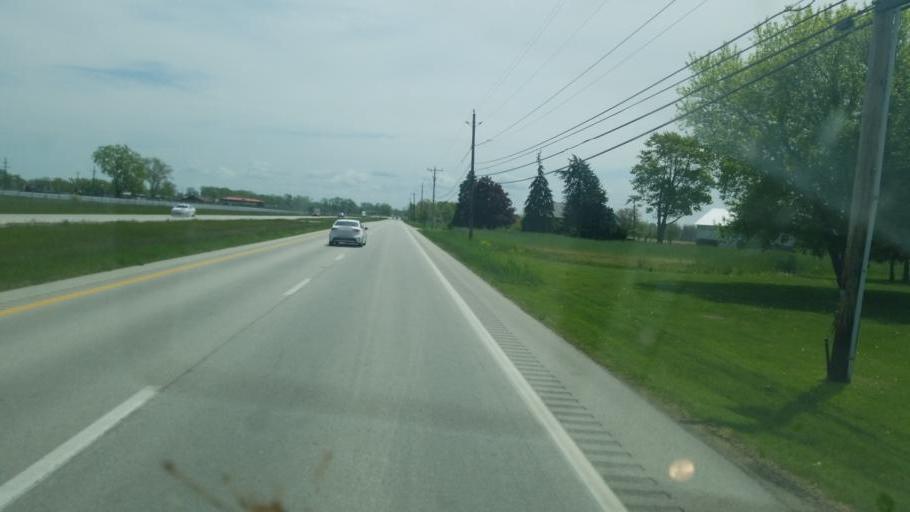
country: US
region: Ohio
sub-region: Ottawa County
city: Port Clinton
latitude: 41.5341
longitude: -83.0290
